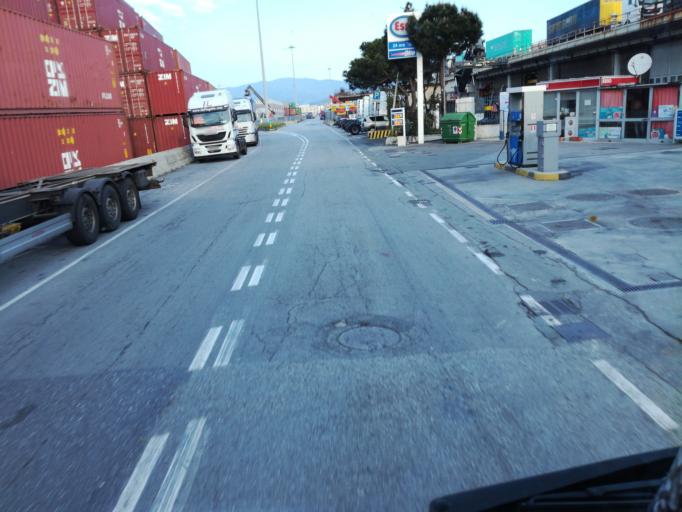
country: IT
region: Liguria
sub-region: Provincia di Genova
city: San Teodoro
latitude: 44.4077
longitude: 8.8935
